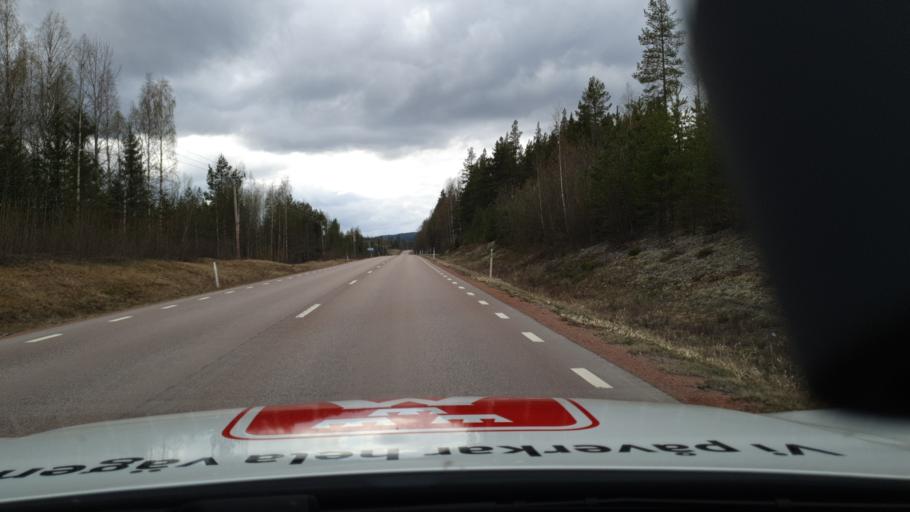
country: SE
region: Jaemtland
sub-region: Braecke Kommun
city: Braecke
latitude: 63.1608
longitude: 15.7163
